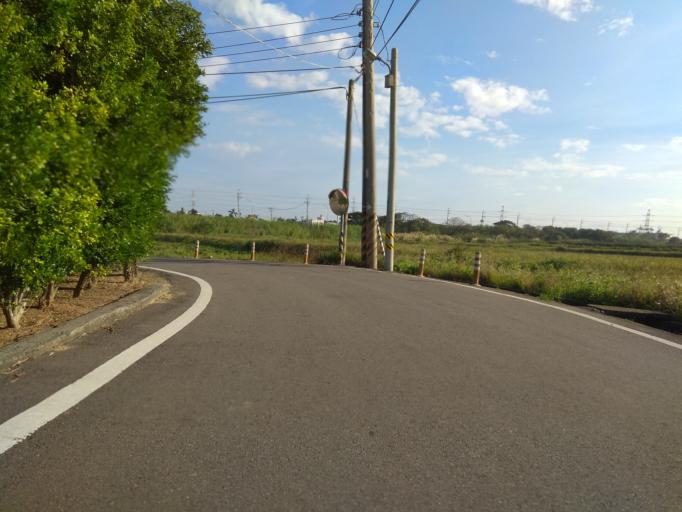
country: TW
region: Taiwan
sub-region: Hsinchu
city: Zhubei
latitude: 24.9816
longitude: 121.0592
